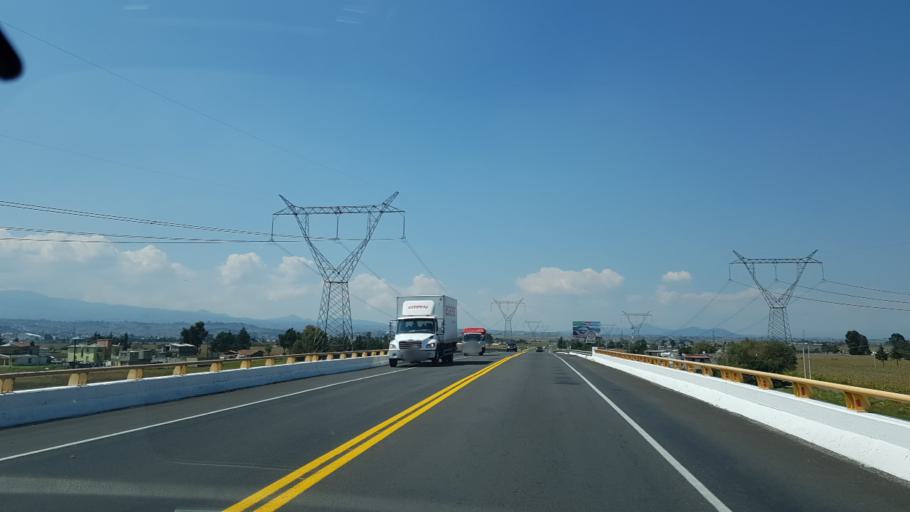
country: MX
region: Mexico
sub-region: Almoloya de Juarez
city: Fraccionamiento Colinas del Sol
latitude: 19.3871
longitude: -99.7403
